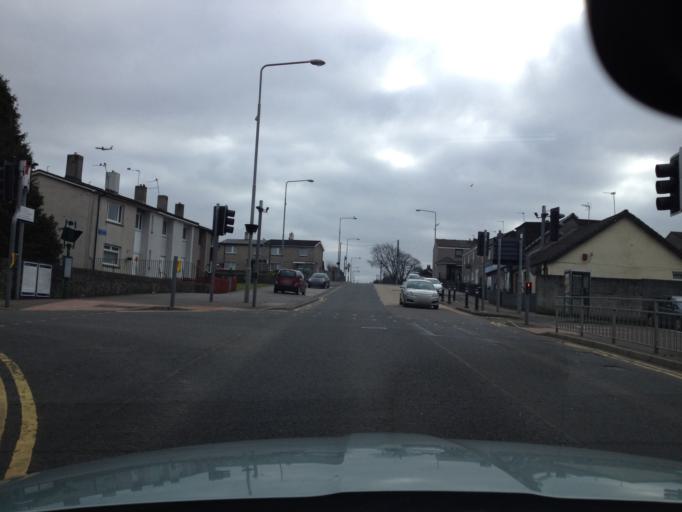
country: GB
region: Scotland
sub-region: West Lothian
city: Livingston
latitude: 55.9184
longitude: -3.5048
